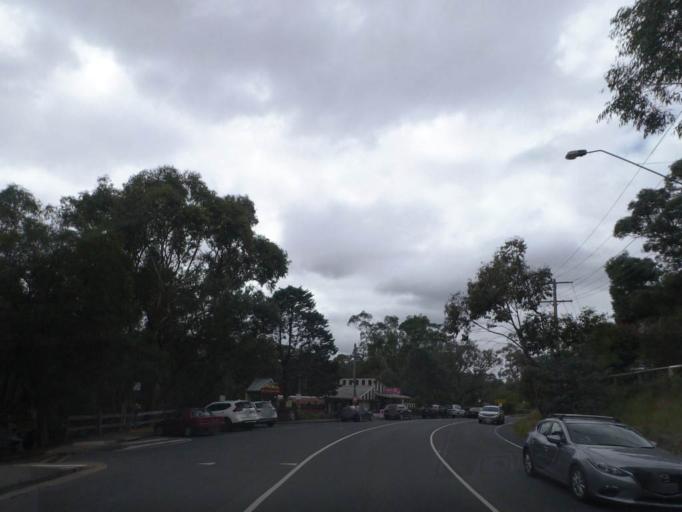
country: AU
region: Victoria
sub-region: Nillumbik
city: North Warrandyte
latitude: -37.7370
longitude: 145.2202
